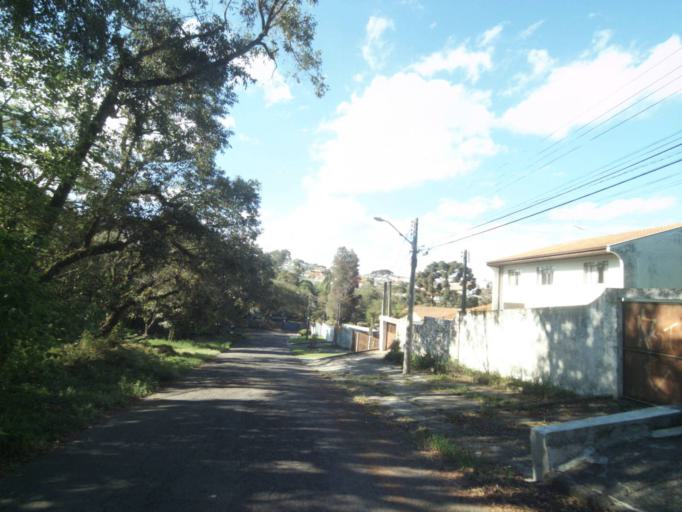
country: BR
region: Parana
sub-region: Curitiba
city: Curitiba
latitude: -25.3880
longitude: -49.2573
